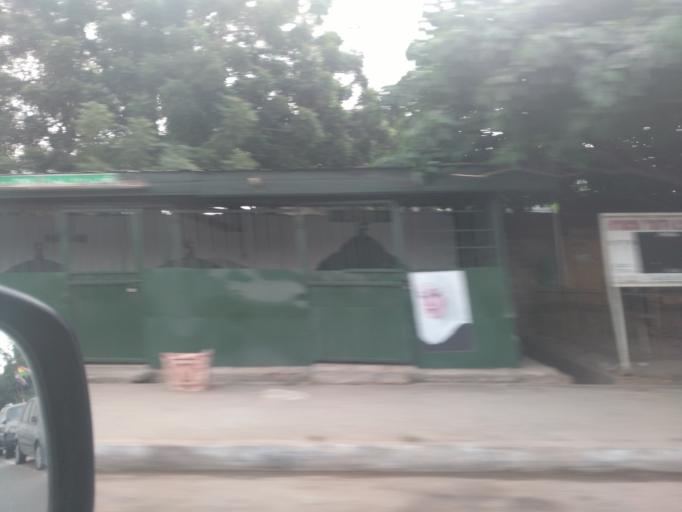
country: GH
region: Greater Accra
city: Accra
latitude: 5.5854
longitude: -0.1931
